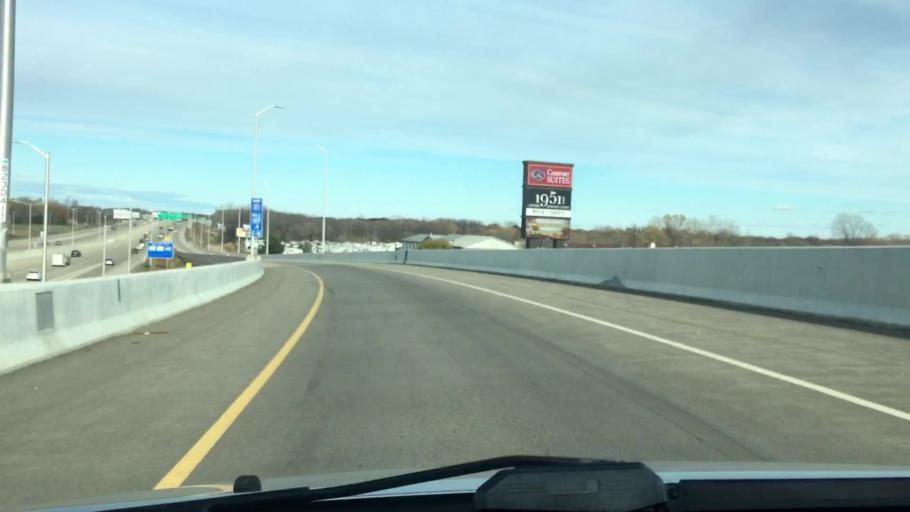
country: US
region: Wisconsin
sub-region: Brown County
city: Howard
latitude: 44.5407
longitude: -88.0747
